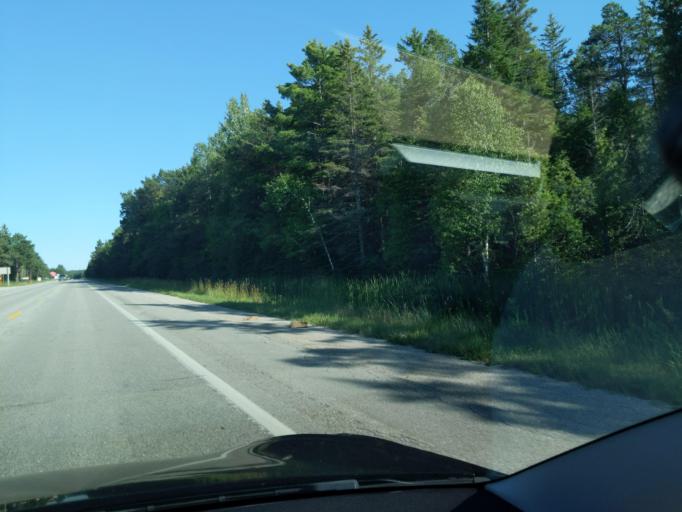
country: US
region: Michigan
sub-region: Mackinac County
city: Saint Ignace
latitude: 45.7585
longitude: -84.7048
